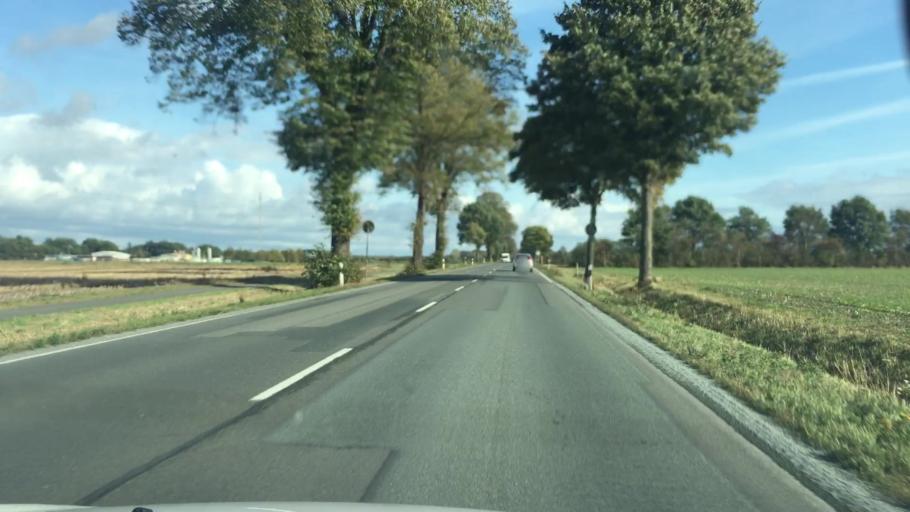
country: DE
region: Lower Saxony
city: Borstel
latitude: 52.6681
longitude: 8.9802
